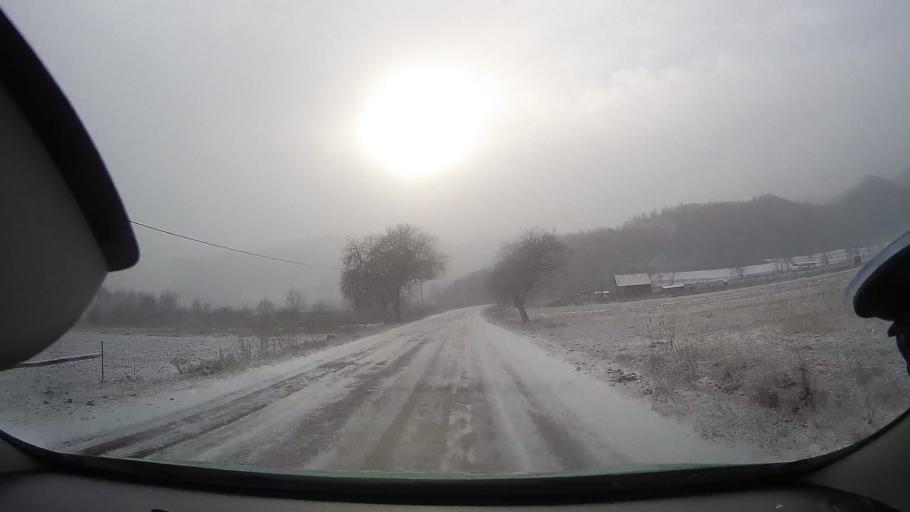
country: RO
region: Alba
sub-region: Comuna Rimetea
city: Rimetea
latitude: 46.3961
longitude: 23.5602
